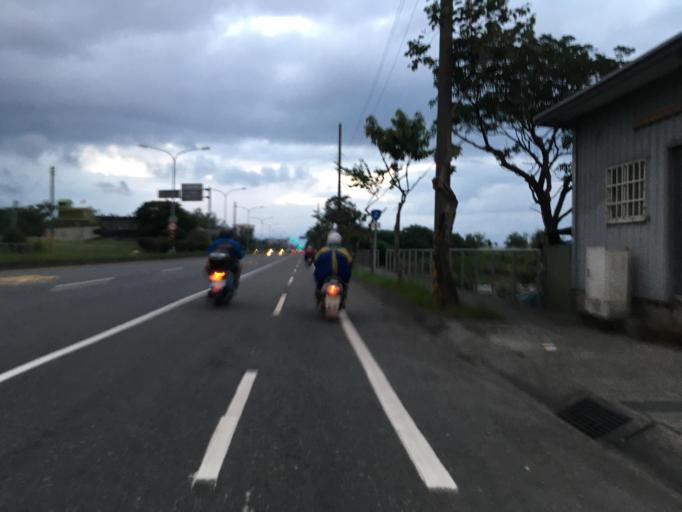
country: TW
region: Taiwan
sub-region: Yilan
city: Yilan
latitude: 24.6175
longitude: 121.8461
